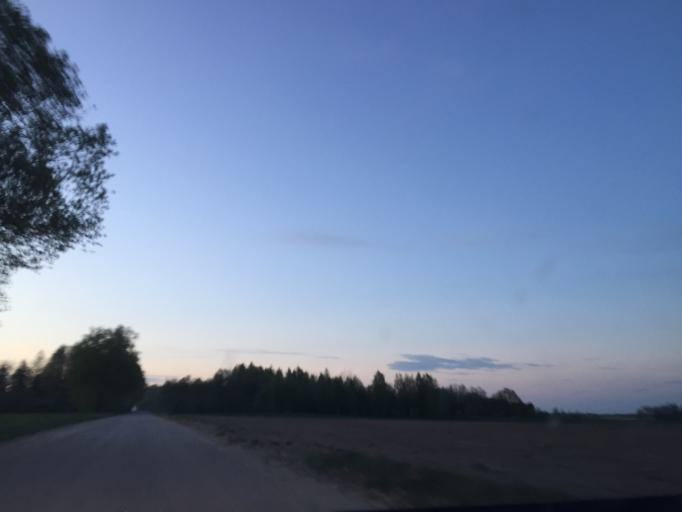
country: LV
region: Bauskas Rajons
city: Bauska
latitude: 56.4881
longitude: 24.1252
